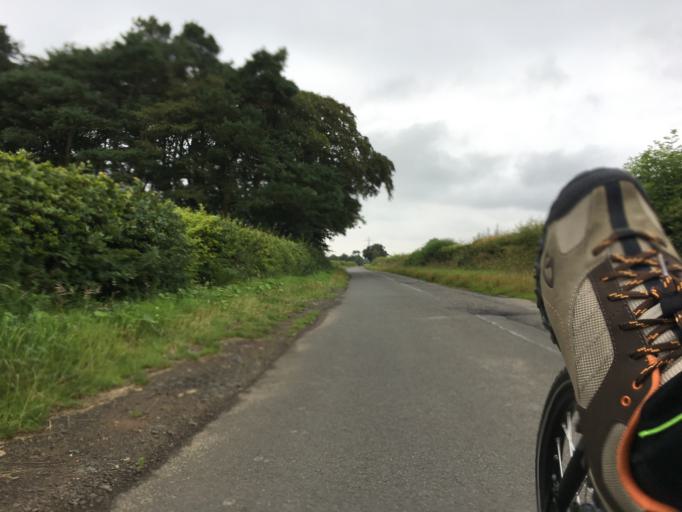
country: GB
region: Scotland
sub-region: West Lothian
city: West Calder
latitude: 55.8461
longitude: -3.5162
